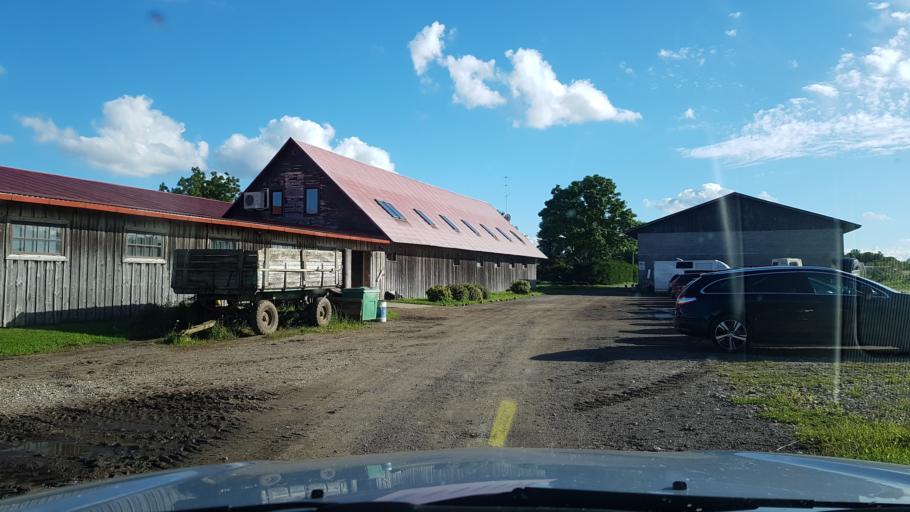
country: EE
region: Harju
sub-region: Kiili vald
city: Kiili
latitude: 59.3446
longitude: 24.8348
